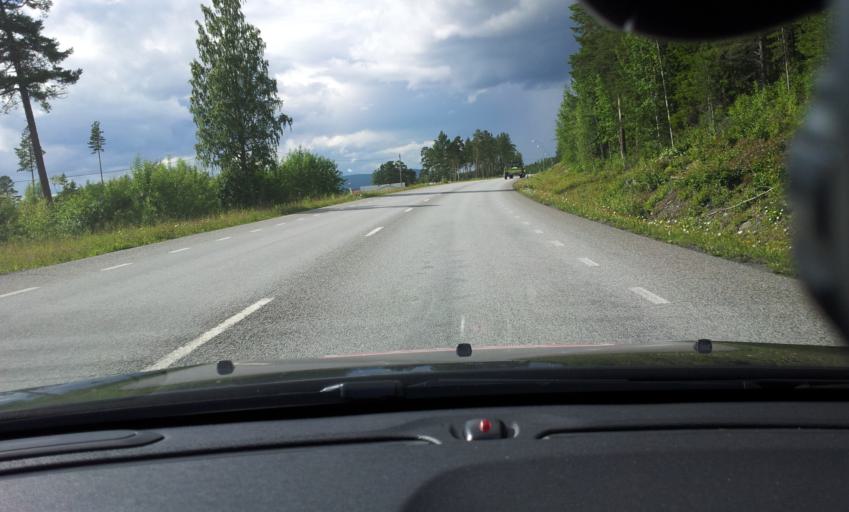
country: SE
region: Jaemtland
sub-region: Are Kommun
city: Jarpen
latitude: 63.3231
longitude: 13.5430
